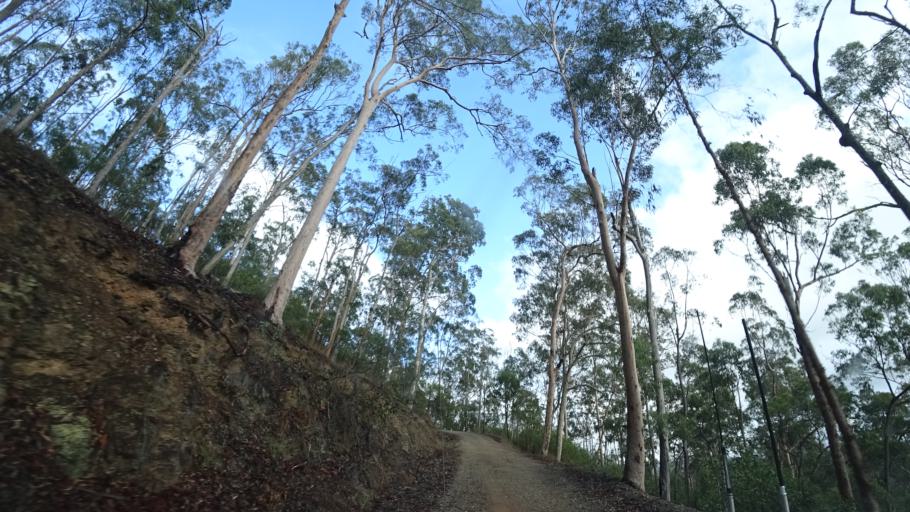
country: AU
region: Queensland
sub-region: Brisbane
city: Kenmore Hills
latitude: -27.4605
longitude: 152.9242
